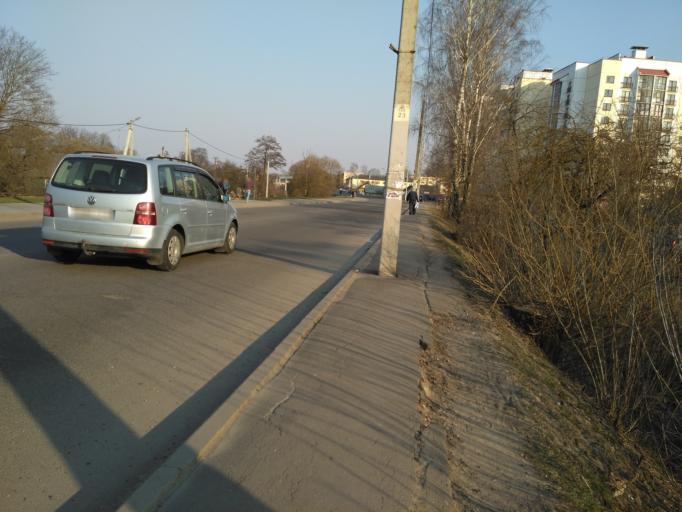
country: BY
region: Minsk
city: Zaslawye
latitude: 54.0094
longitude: 27.2743
